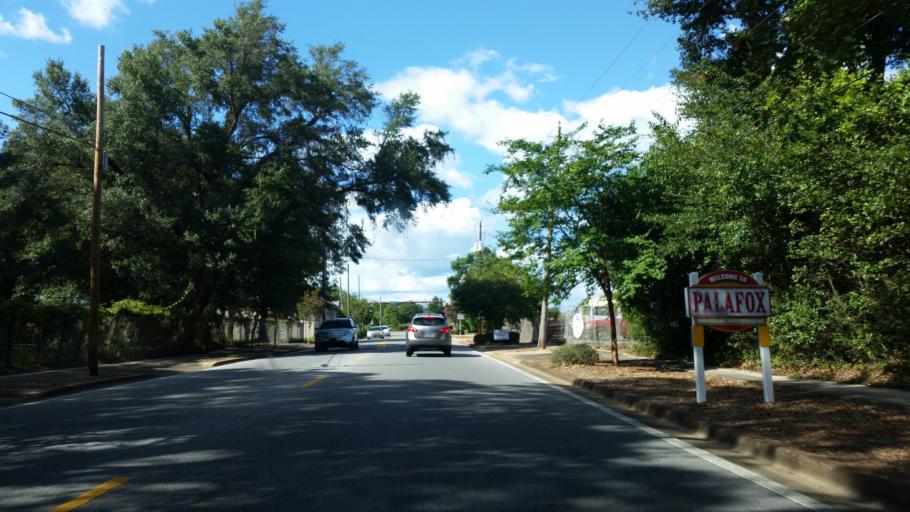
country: US
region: Florida
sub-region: Escambia County
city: Goulding
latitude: 30.4436
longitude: -87.2287
